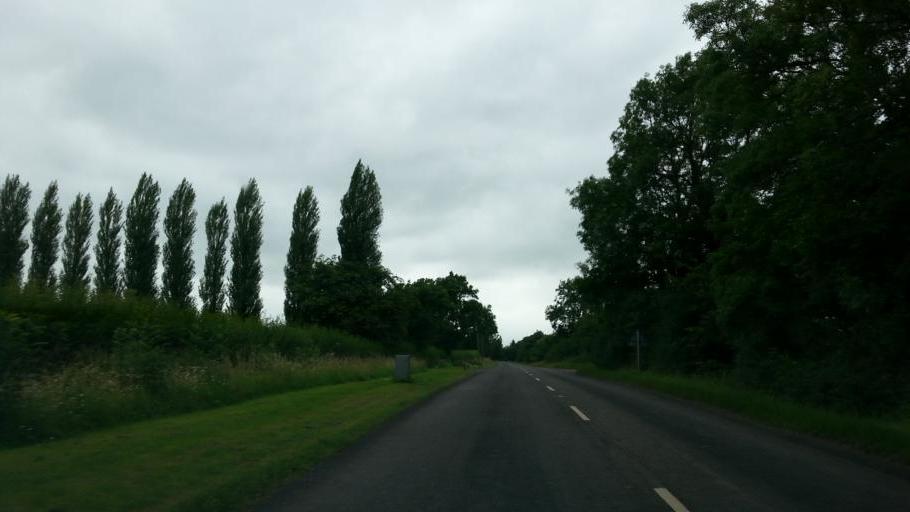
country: GB
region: England
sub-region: Nottinghamshire
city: Farnsfield
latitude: 53.0636
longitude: -1.0175
